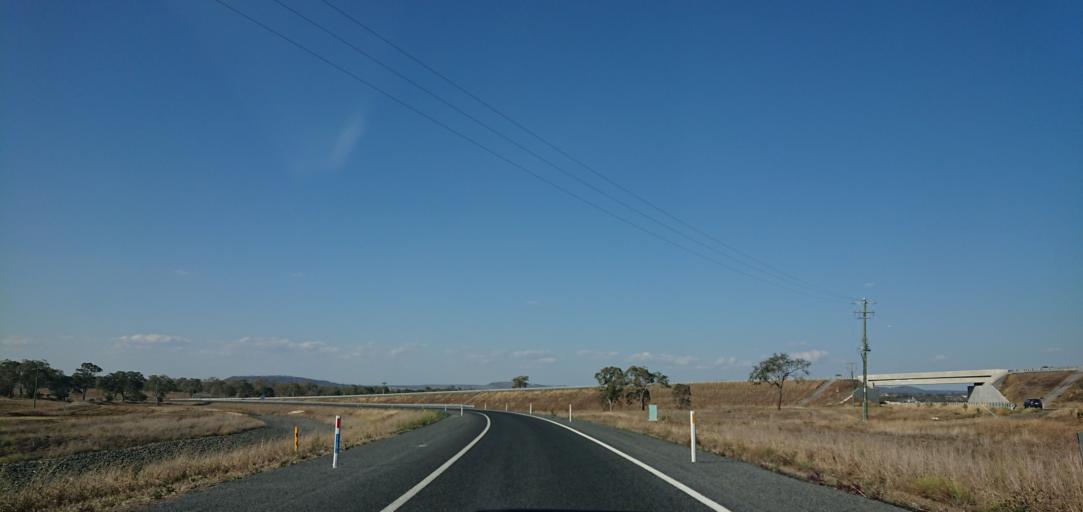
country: AU
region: Queensland
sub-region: Toowoomba
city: Westbrook
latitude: -27.6154
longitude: 151.7835
